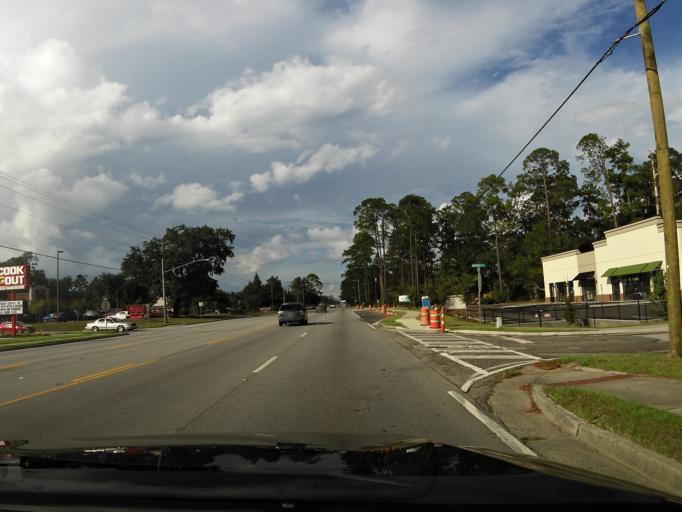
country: US
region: Georgia
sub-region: Liberty County
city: Hinesville
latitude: 31.8297
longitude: -81.5975
